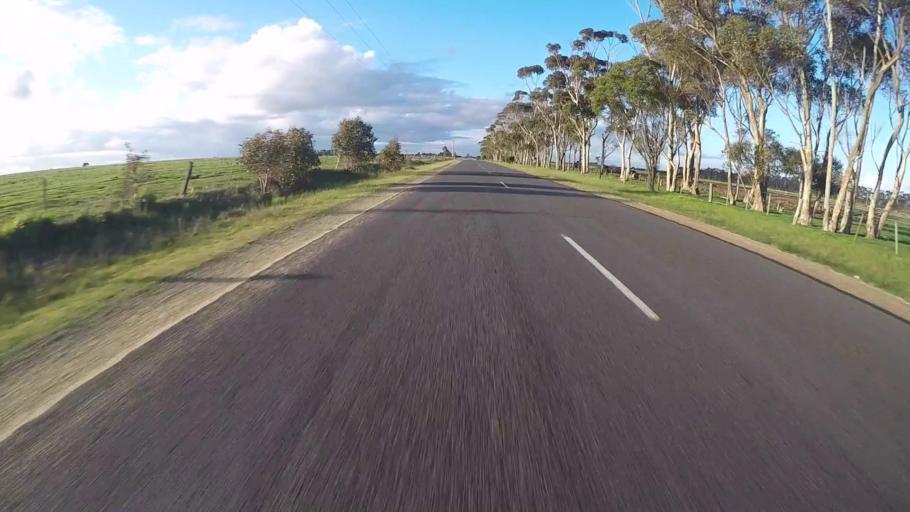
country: AU
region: Victoria
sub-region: Greater Geelong
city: Wandana Heights
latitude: -38.1270
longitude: 144.2040
